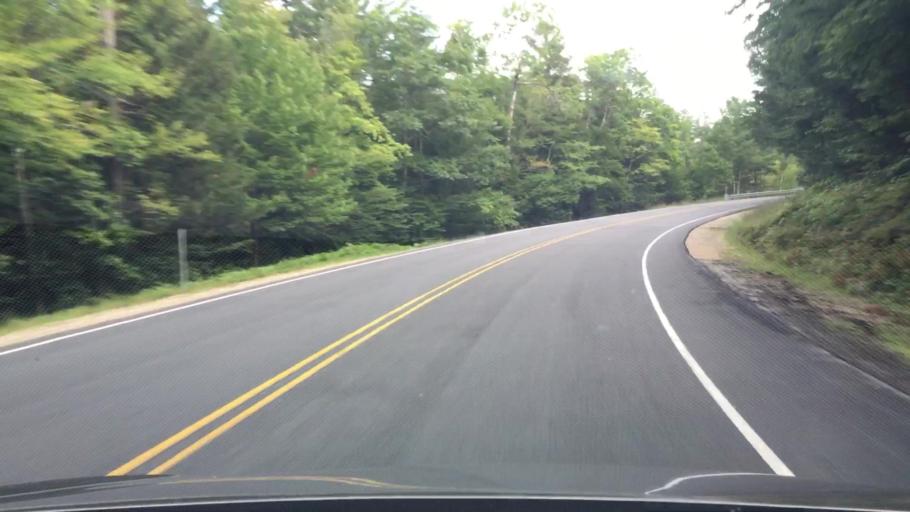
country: US
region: New Hampshire
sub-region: Carroll County
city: Conway
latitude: 44.0005
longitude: -71.2309
